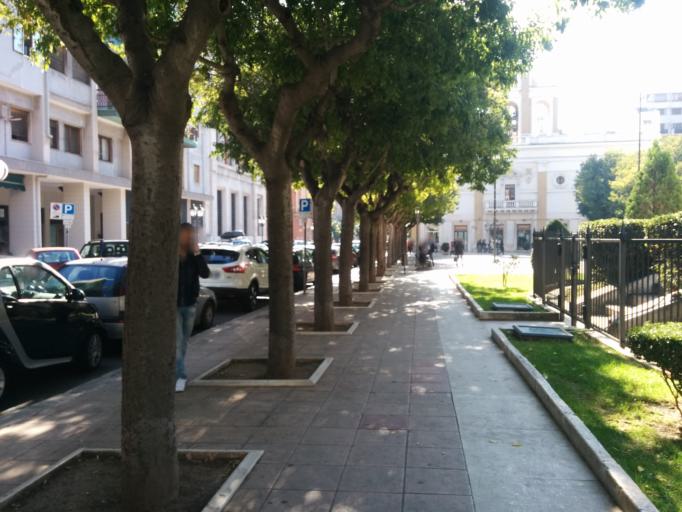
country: IT
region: Apulia
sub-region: Provincia di Taranto
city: Taranto
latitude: 40.4724
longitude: 17.2401
